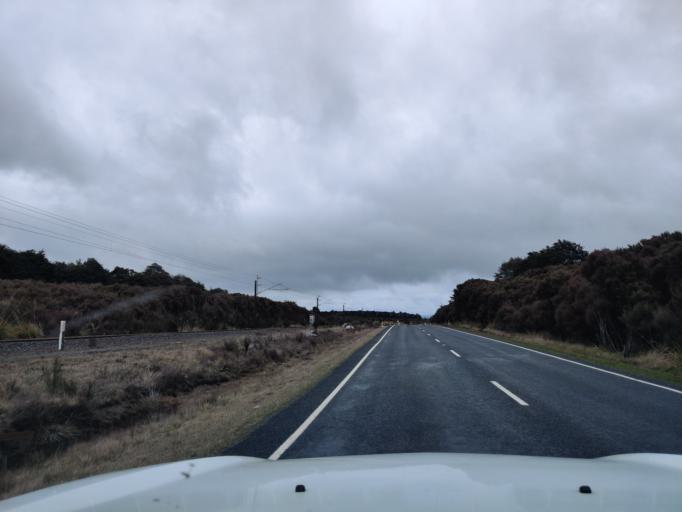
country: NZ
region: Manawatu-Wanganui
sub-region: Ruapehu District
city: Waiouru
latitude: -39.3209
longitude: 175.3859
